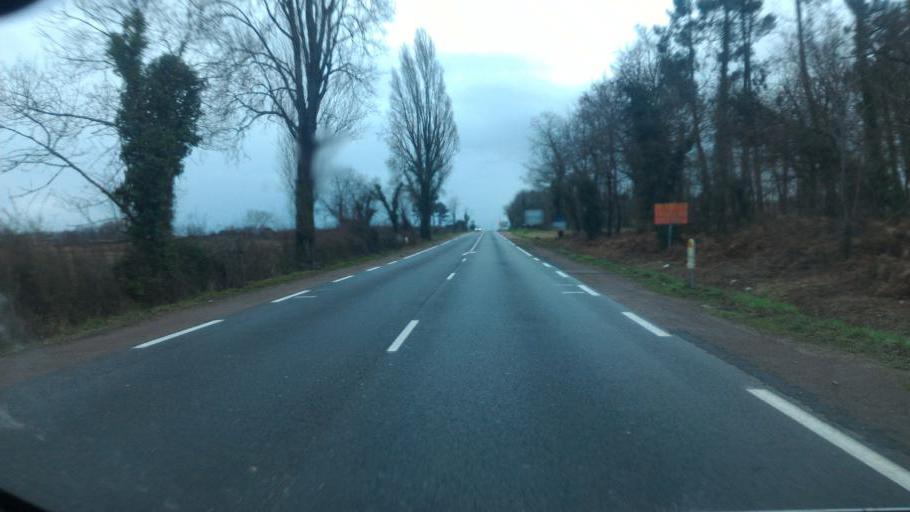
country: FR
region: Aquitaine
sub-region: Departement de la Gironde
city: Saint-Gervais
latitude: 45.0099
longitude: -0.4399
